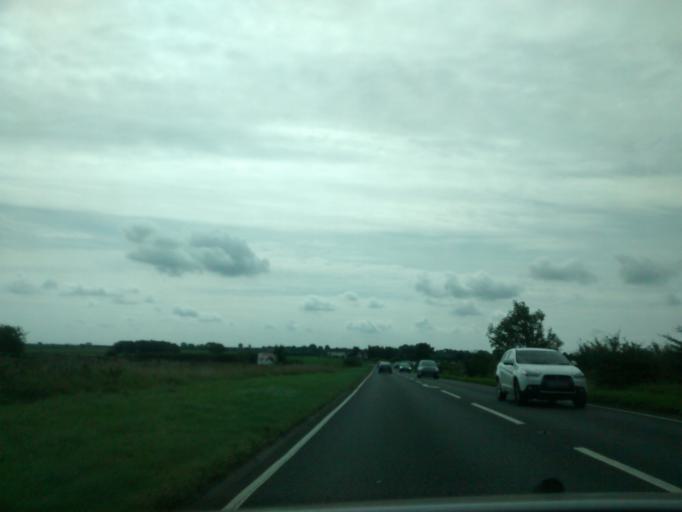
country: GB
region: England
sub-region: South Gloucestershire
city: Cold Ashton
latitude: 51.4674
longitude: -2.3655
